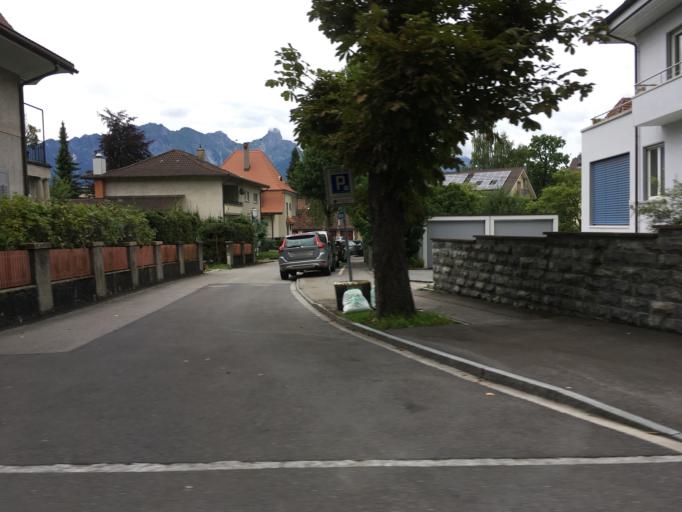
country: CH
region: Bern
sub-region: Thun District
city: Thun
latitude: 46.7500
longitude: 7.6378
